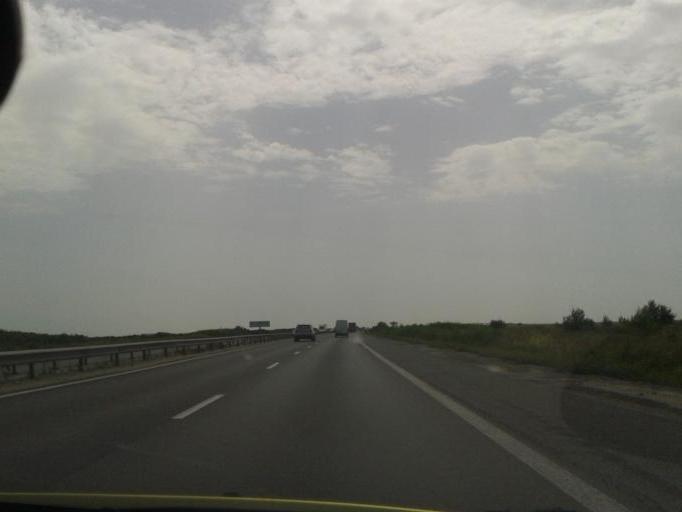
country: RO
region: Dambovita
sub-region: Comuna Morteni
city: Morteni
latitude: 44.6975
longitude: 25.2435
